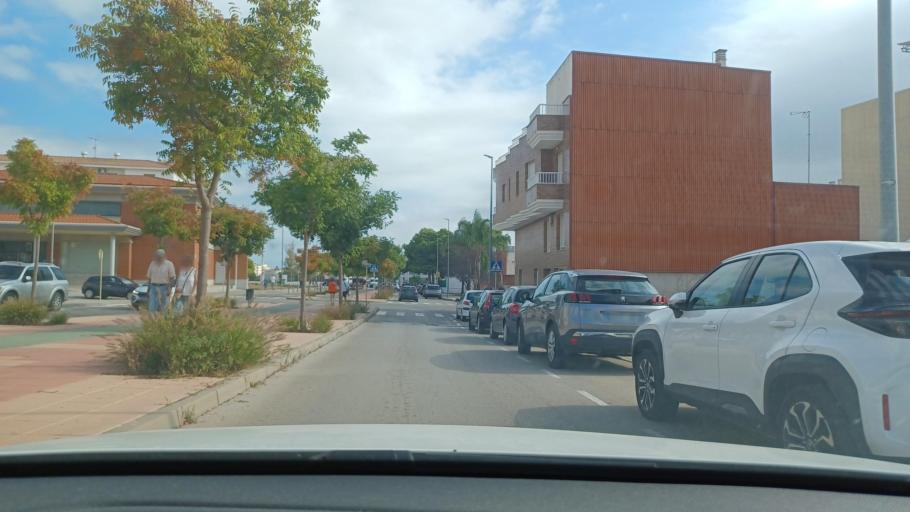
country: ES
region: Catalonia
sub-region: Provincia de Tarragona
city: Sant Carles de la Rapita
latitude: 40.6179
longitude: 0.5857
